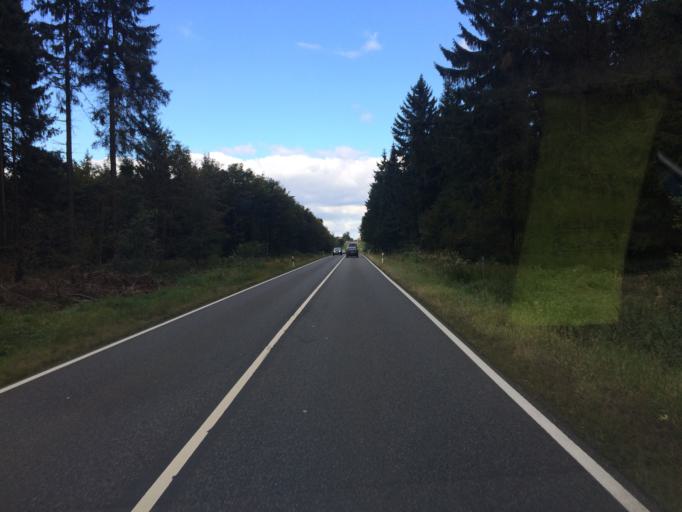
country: DE
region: Rheinland-Pfalz
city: Stein-Neukirch
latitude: 50.6963
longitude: 8.0645
